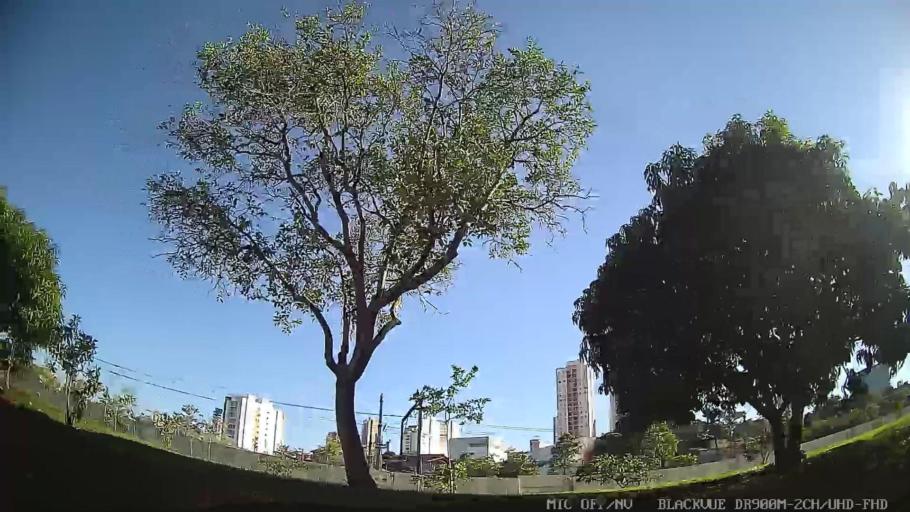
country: BR
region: Sao Paulo
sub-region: Guarulhos
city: Guarulhos
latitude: -23.5310
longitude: -46.5233
